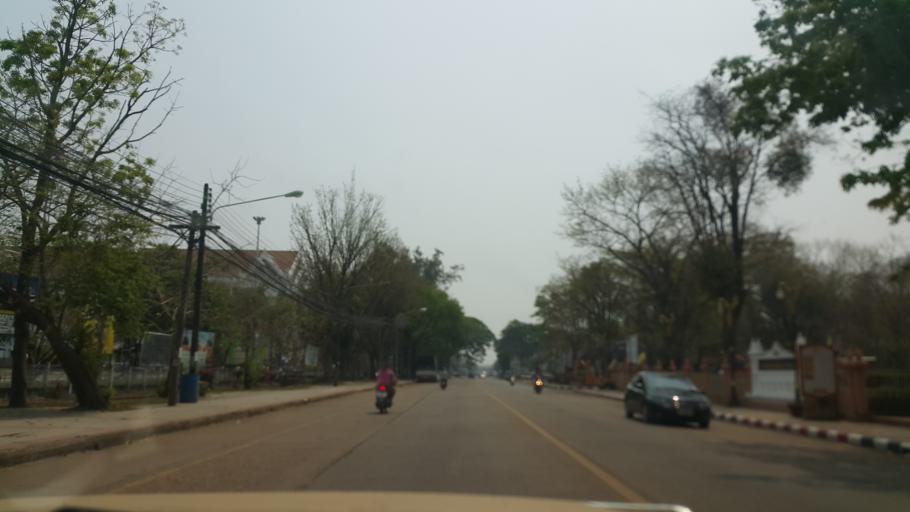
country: TH
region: Nakhon Phanom
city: Nakhon Phanom
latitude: 17.4085
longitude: 104.7807
